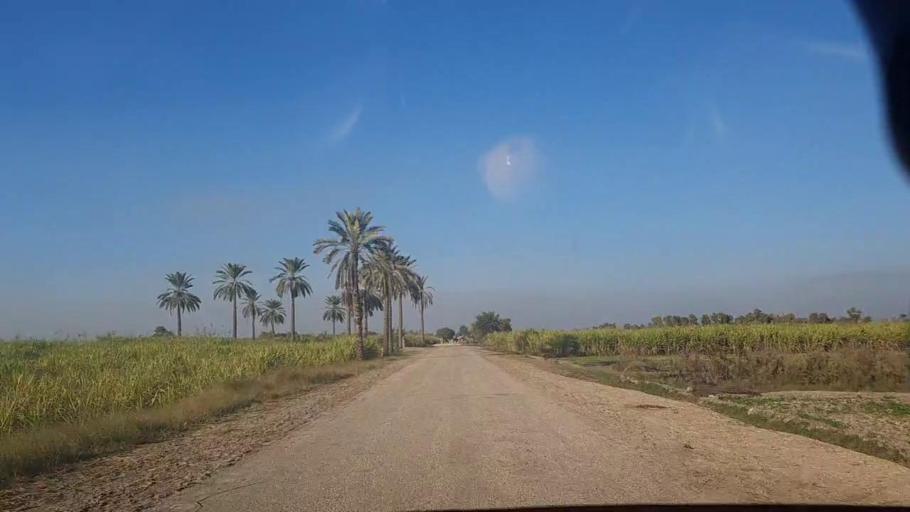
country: PK
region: Sindh
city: Sobhadero
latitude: 27.4099
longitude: 68.4224
